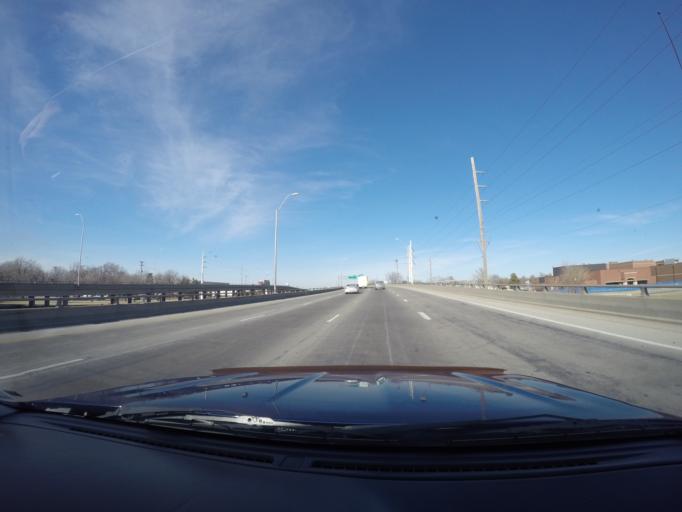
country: US
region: Kansas
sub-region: Sedgwick County
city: Wichita
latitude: 37.6838
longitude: -97.3123
